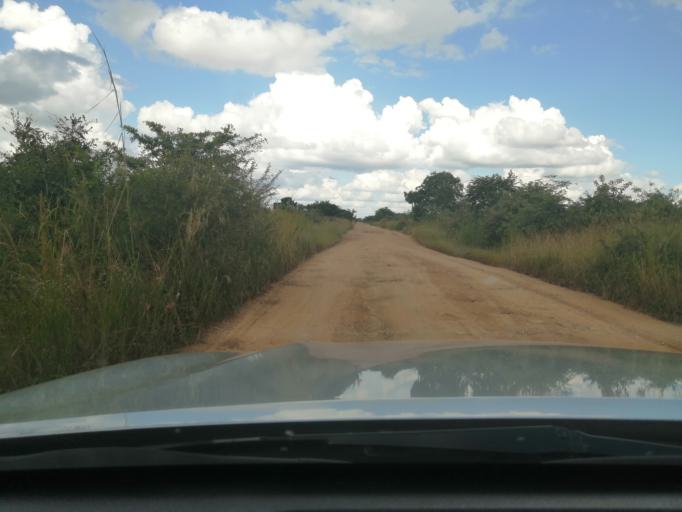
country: ZM
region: Lusaka
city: Lusaka
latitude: -15.2116
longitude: 28.0964
